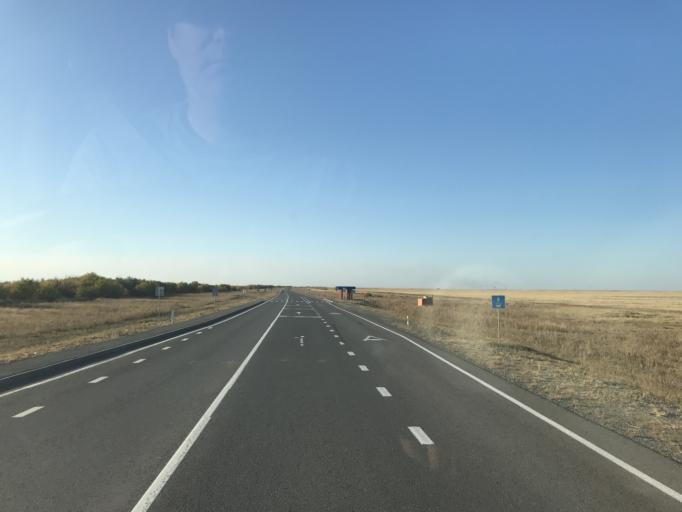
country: KZ
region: Pavlodar
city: Aksu
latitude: 52.0190
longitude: 77.2317
